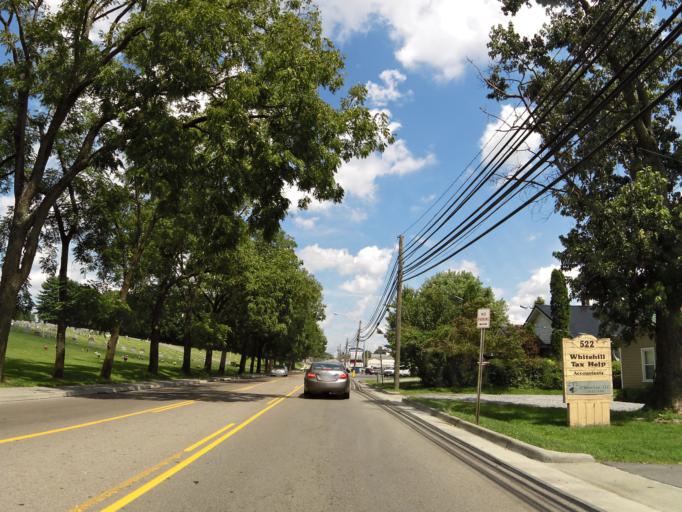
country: US
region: Virginia
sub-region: Washington County
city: Abingdon
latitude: 36.7154
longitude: -81.9602
